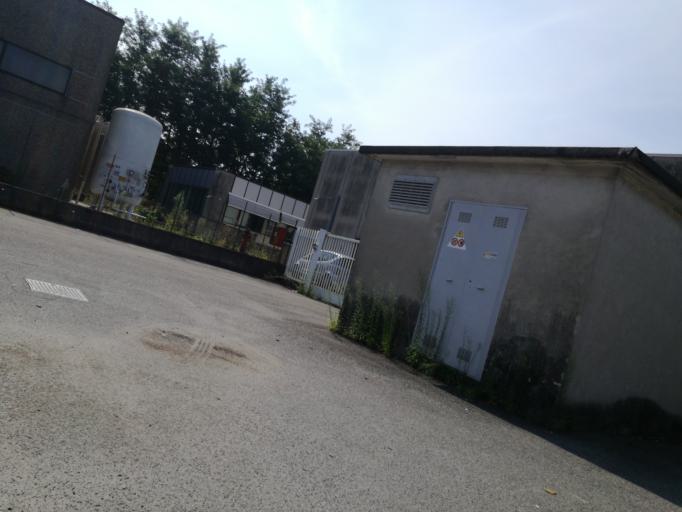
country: IT
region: Lombardy
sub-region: Provincia di Lecco
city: Verderio Inferiore
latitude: 45.6640
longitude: 9.4226
